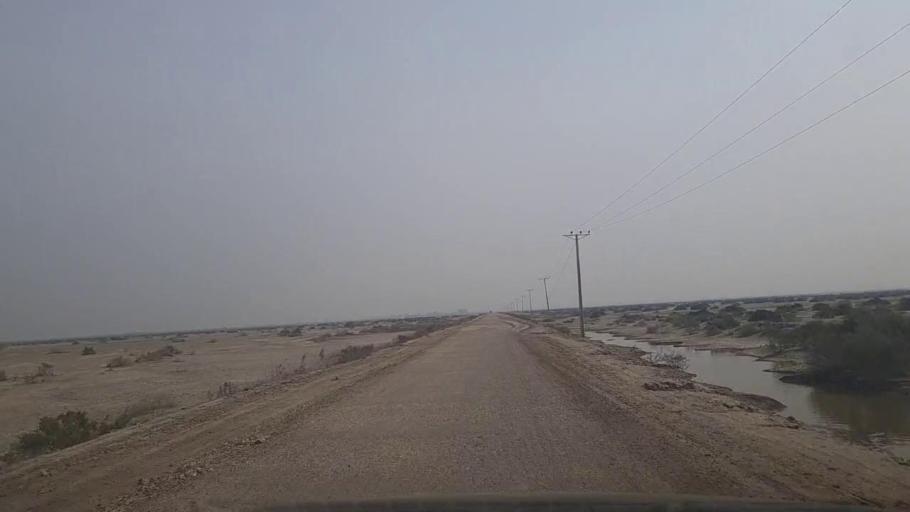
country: PK
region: Sindh
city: Mirpur Sakro
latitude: 24.4681
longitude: 67.6798
